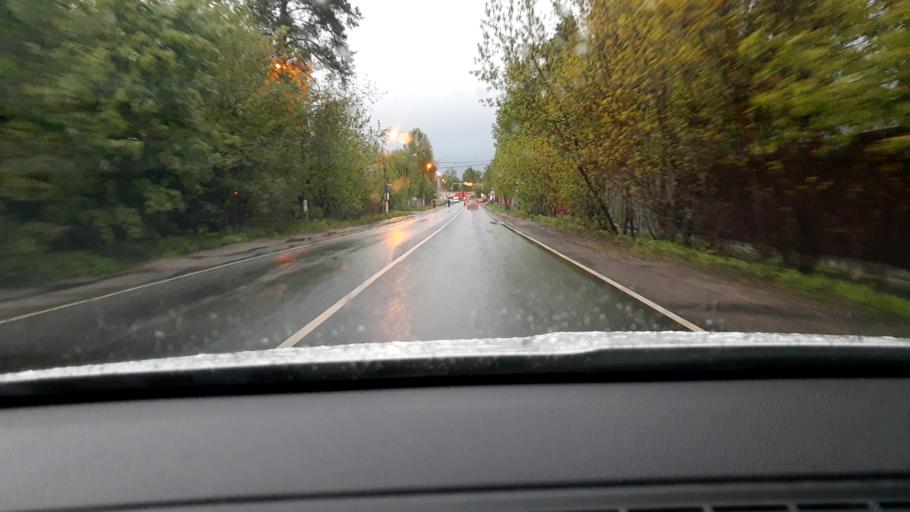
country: RU
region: Moskovskaya
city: Zagoryanskiy
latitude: 55.9230
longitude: 37.9146
